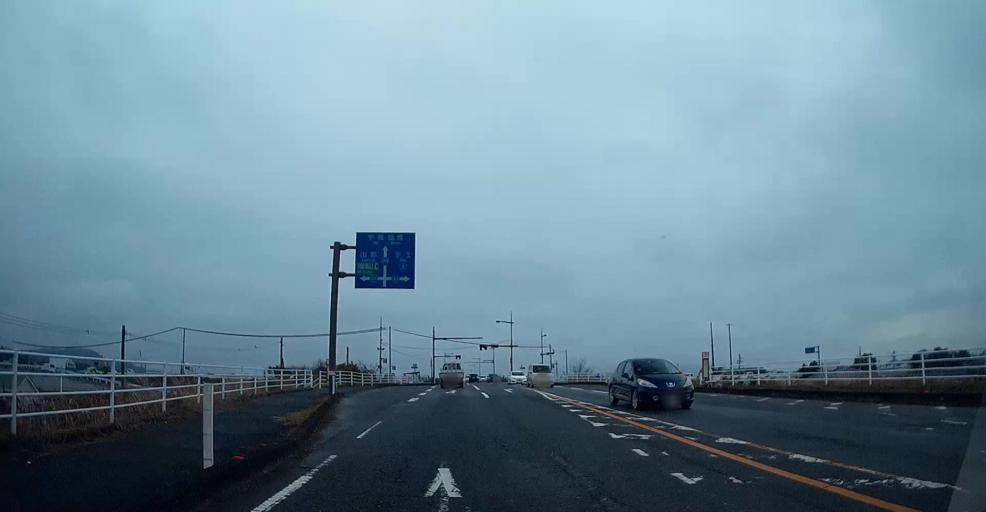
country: JP
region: Kumamoto
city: Kumamoto
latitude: 32.7388
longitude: 130.7403
